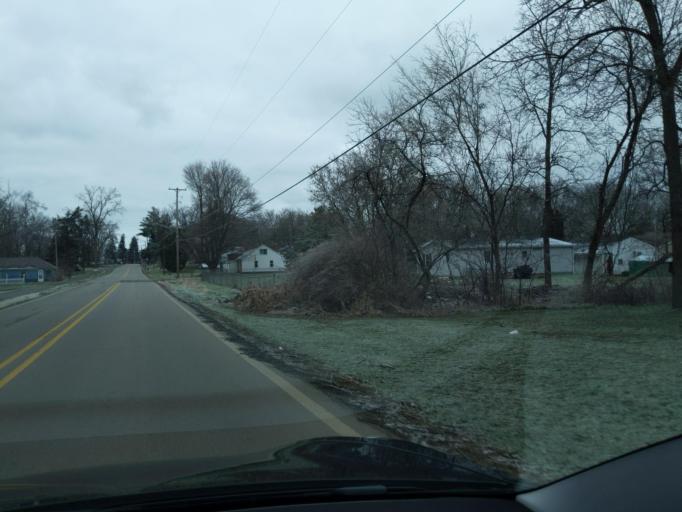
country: US
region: Michigan
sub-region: Jackson County
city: Spring Arbor
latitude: 42.2009
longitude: -84.5537
